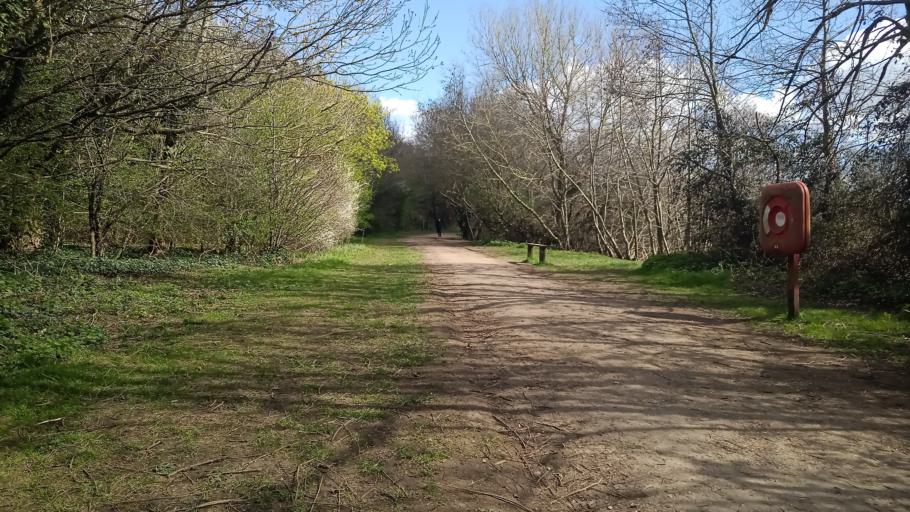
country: GB
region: England
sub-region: Oxfordshire
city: Ducklington
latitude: 51.7751
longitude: -1.4826
